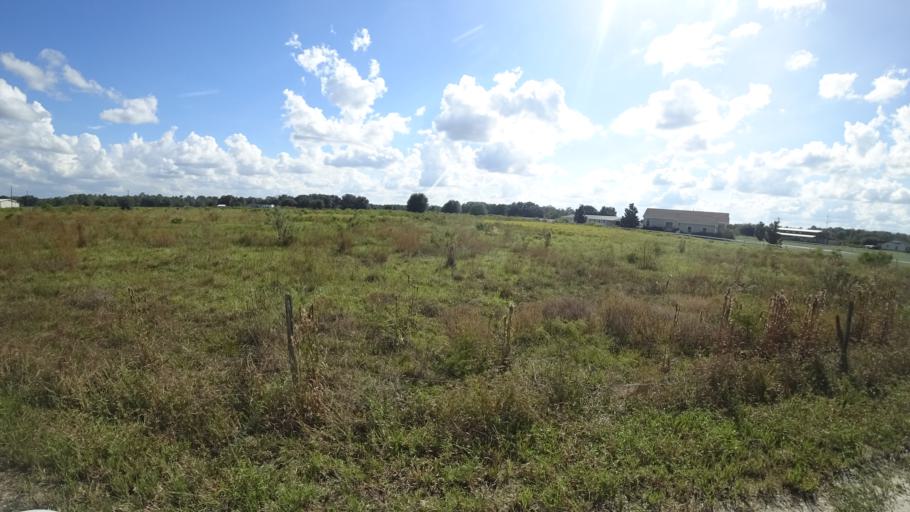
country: US
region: Florida
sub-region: Hardee County
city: Wauchula
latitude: 27.4898
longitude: -82.0690
